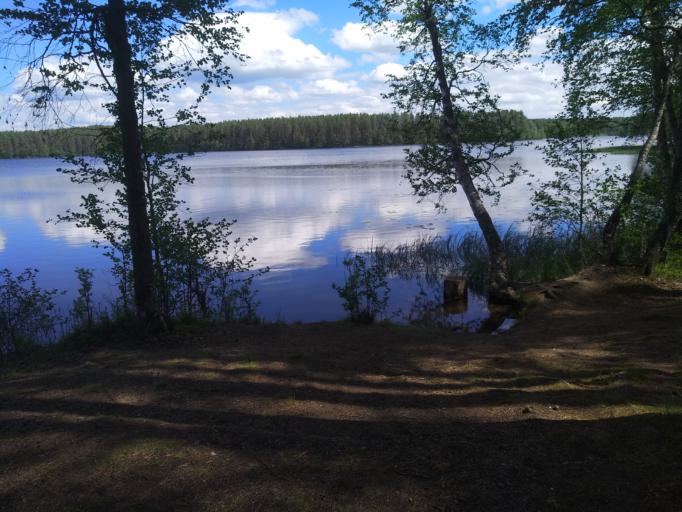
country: RU
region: Leningrad
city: Michurinskoye
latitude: 60.5906
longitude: 29.8688
